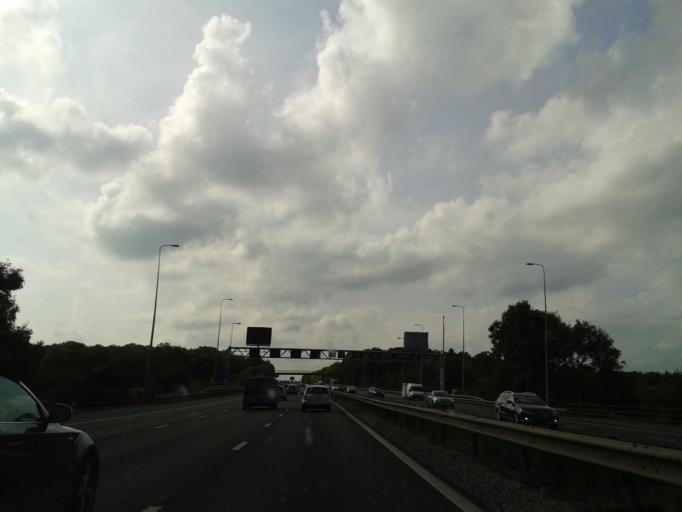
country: GB
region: England
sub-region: Solihull
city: Solihull
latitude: 52.3910
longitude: -1.7731
